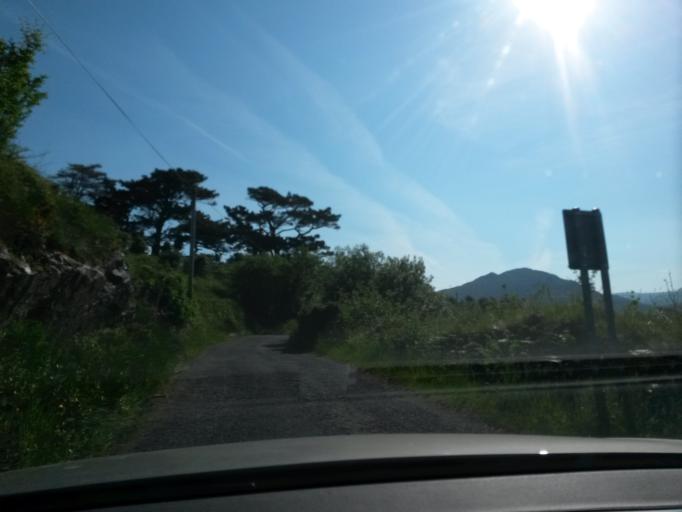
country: IE
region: Munster
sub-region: Ciarrai
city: Kenmare
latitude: 51.7835
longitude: -9.8189
